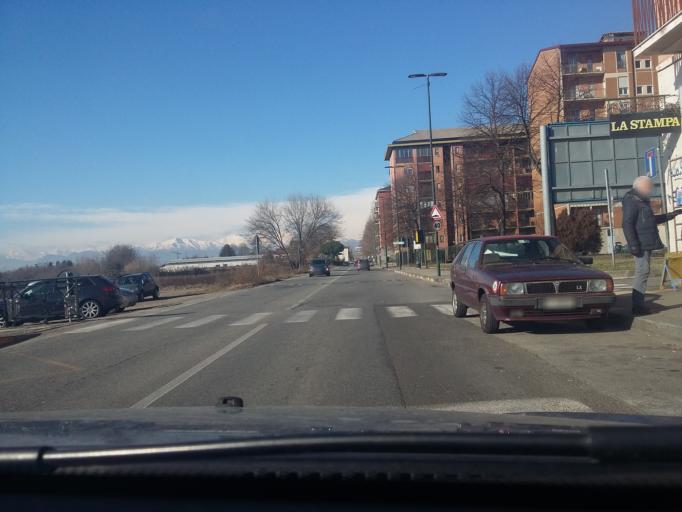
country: IT
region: Piedmont
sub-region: Provincia di Torino
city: Nichelino
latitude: 45.0113
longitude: 7.6337
